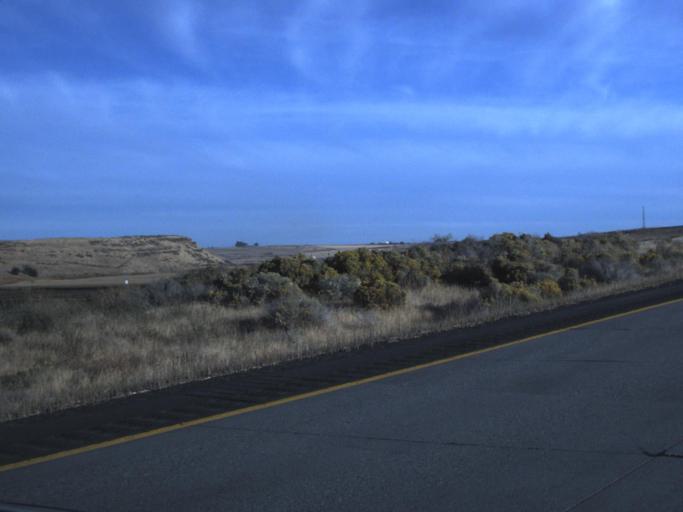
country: US
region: Washington
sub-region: Franklin County
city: Basin City
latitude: 46.5539
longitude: -119.0007
